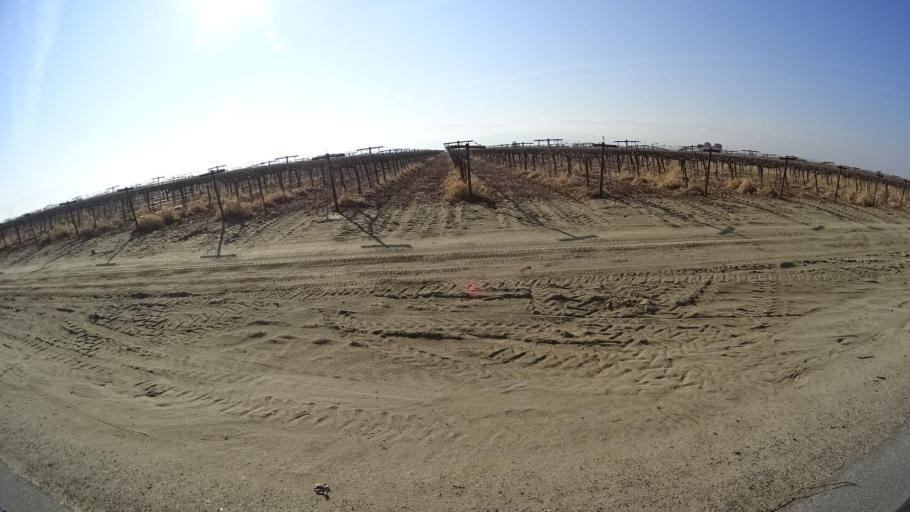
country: US
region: California
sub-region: Kern County
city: Weedpatch
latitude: 35.1220
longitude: -118.9811
